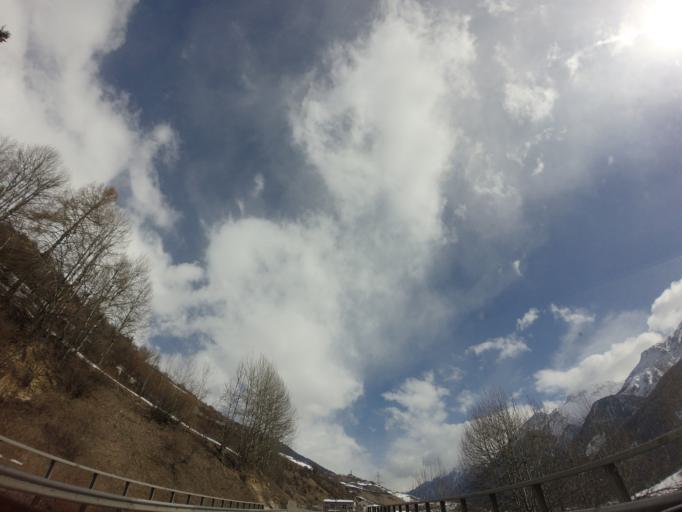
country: CH
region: Grisons
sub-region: Inn District
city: Scuol
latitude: 46.8041
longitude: 10.3157
